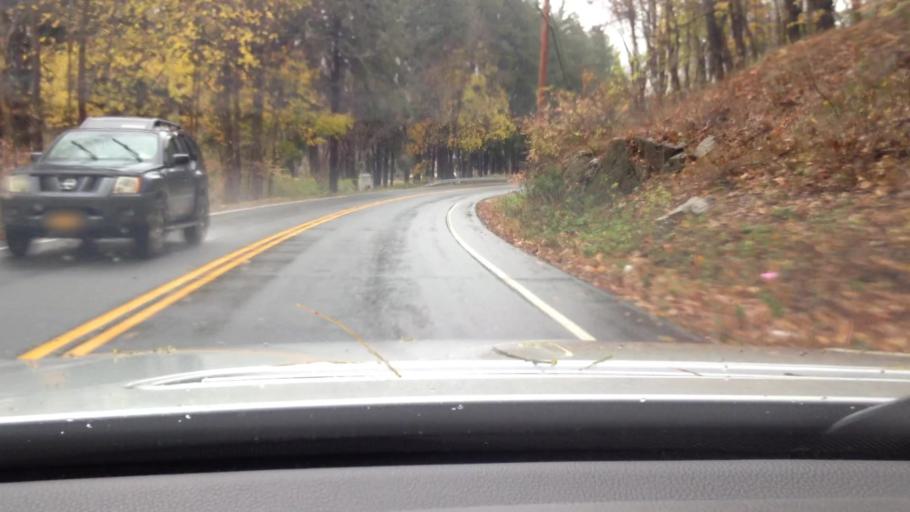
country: US
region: New York
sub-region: Putnam County
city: Cold Spring
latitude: 41.4170
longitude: -73.9394
